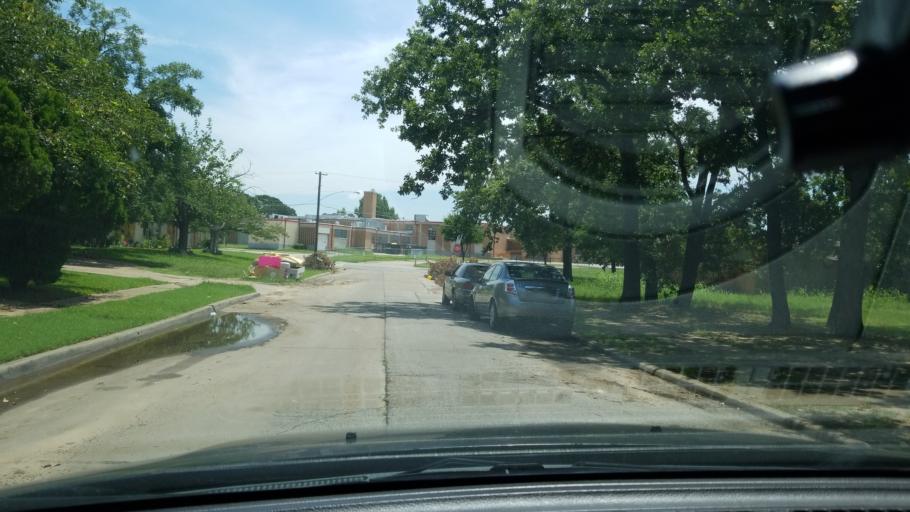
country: US
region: Texas
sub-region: Dallas County
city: Balch Springs
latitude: 32.7408
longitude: -96.6431
